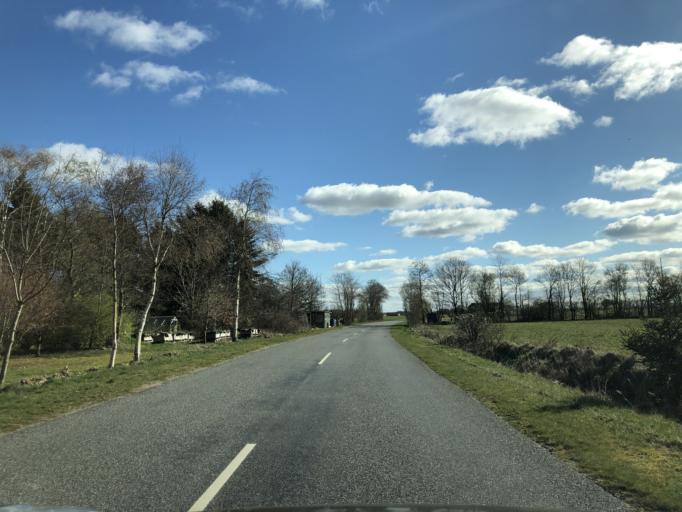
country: DK
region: North Denmark
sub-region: Vesthimmerland Kommune
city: Alestrup
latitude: 56.6094
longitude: 9.5887
